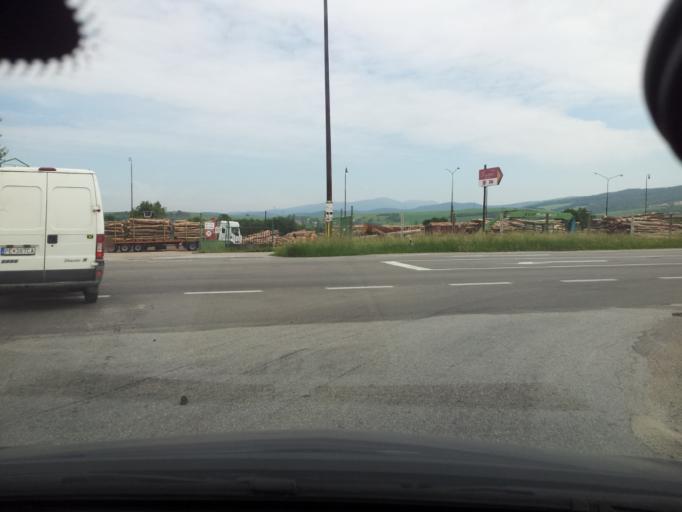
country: SK
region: Nitriansky
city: Partizanske
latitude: 48.6252
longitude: 18.4276
